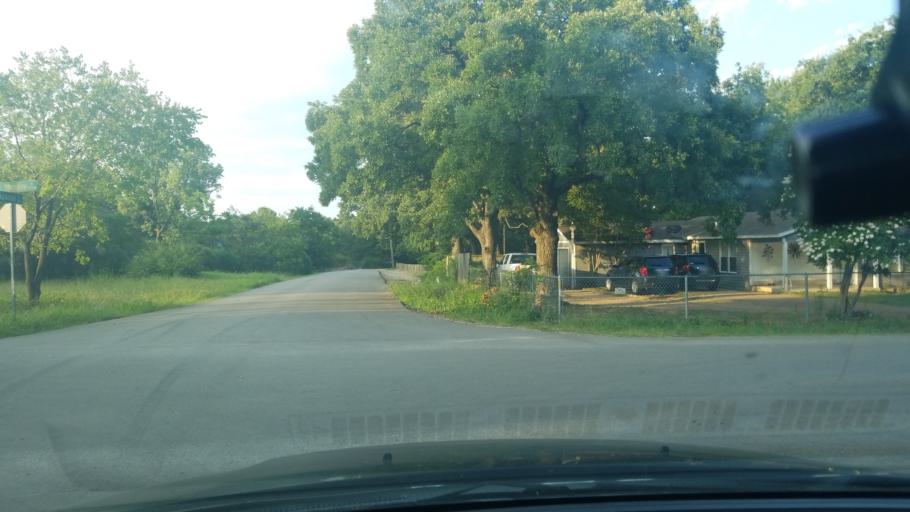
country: US
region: Texas
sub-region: Dallas County
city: Balch Springs
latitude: 32.7238
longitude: -96.6527
